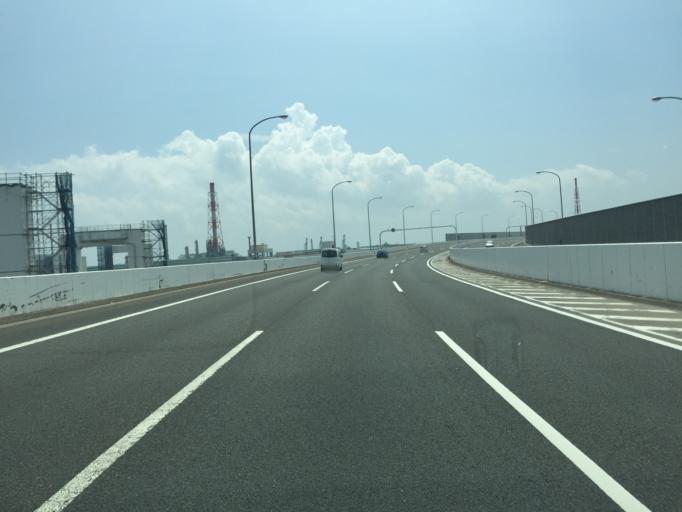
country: JP
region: Kanagawa
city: Yokohama
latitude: 35.4180
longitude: 139.6704
